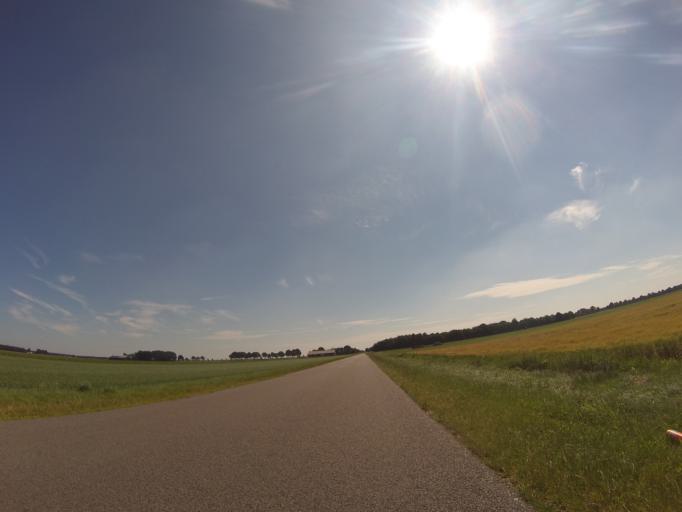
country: NL
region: Drenthe
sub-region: Gemeente Emmen
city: Klazienaveen
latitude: 52.6890
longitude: 6.9681
